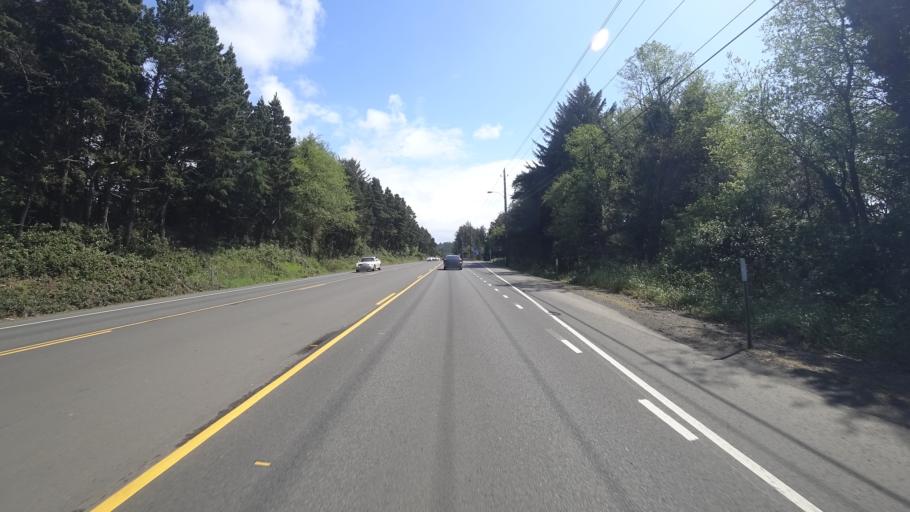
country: US
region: Oregon
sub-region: Lincoln County
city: Newport
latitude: 44.6660
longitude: -124.0565
